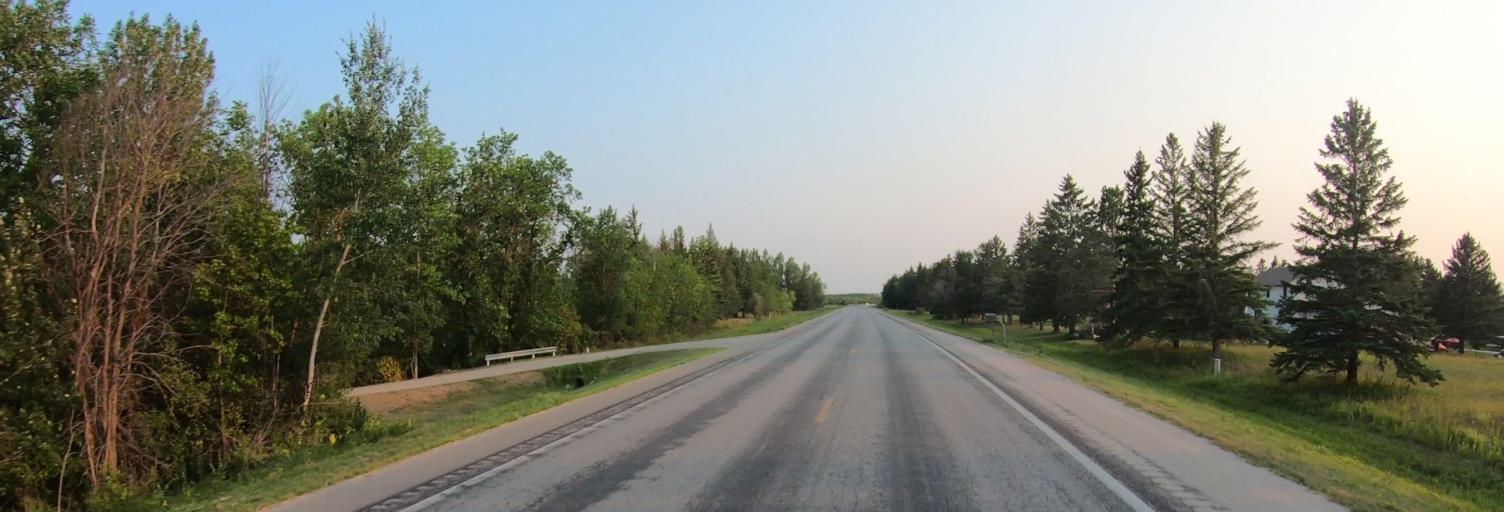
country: US
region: Minnesota
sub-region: Roseau County
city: Warroad
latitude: 48.8781
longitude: -95.3204
